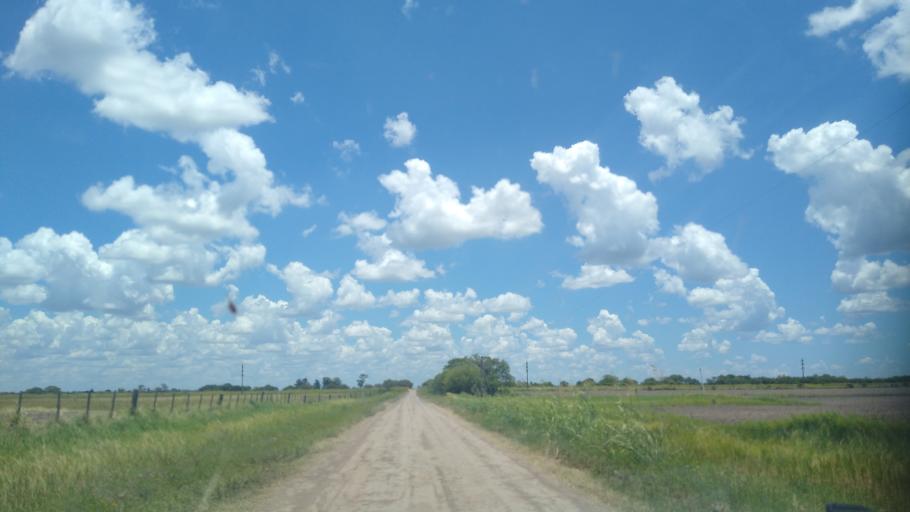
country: AR
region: Chaco
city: Presidencia Roque Saenz Pena
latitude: -26.7331
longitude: -60.3799
